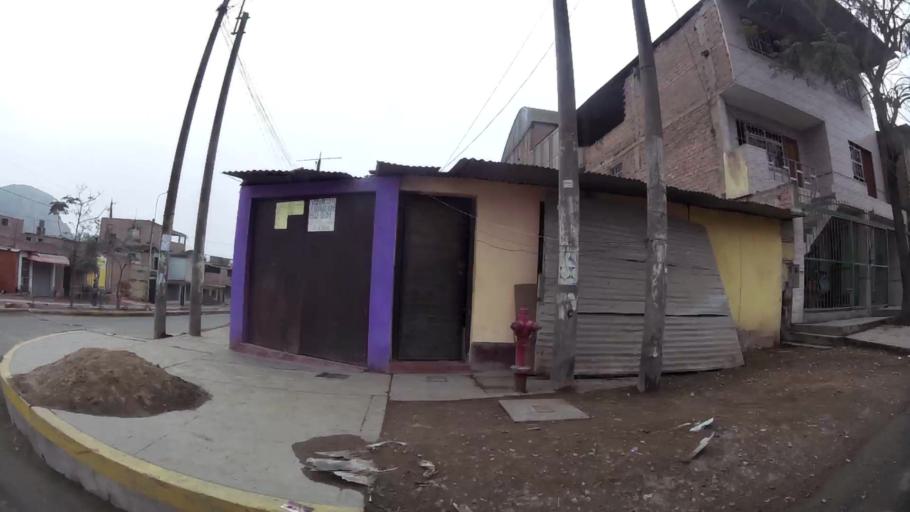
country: PE
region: Lima
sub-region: Lima
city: Surco
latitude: -12.1829
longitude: -76.9250
